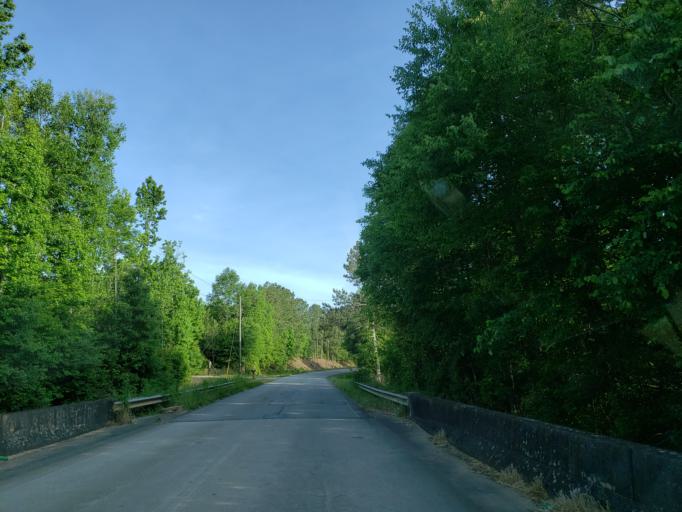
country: US
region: Georgia
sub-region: Carroll County
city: Bowdon
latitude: 33.4838
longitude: -85.3018
